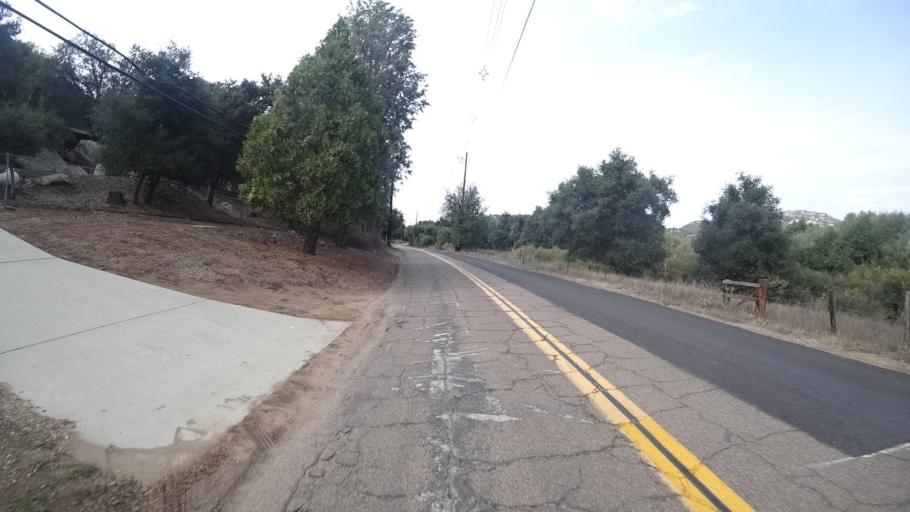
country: US
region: California
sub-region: San Diego County
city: Descanso
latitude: 32.8601
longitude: -116.6175
